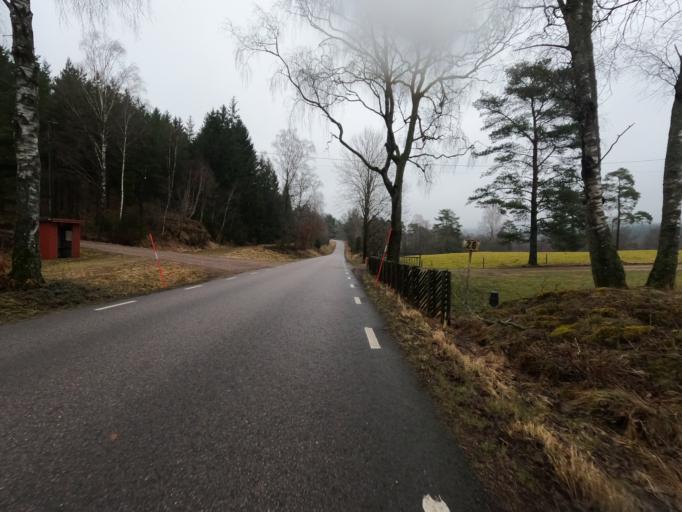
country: SE
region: Halland
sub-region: Hylte Kommun
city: Torup
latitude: 56.7786
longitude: 13.1828
